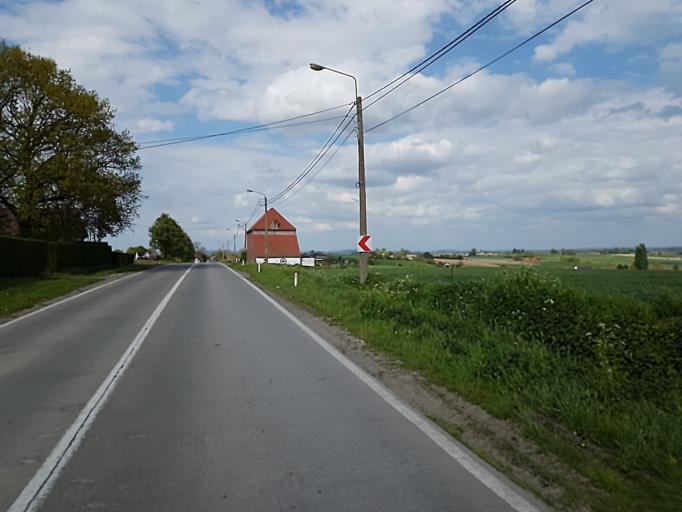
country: BE
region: Wallonia
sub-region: Province du Hainaut
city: Tournai
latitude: 50.6530
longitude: 3.4326
